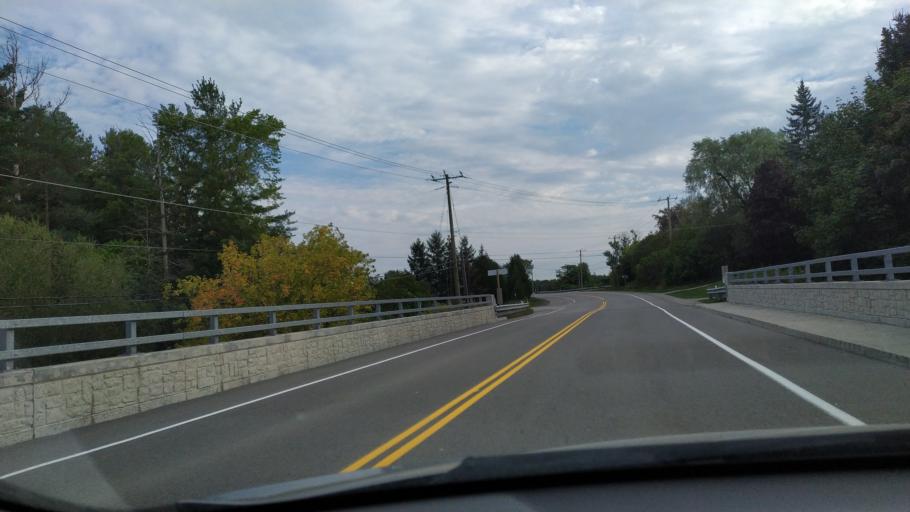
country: CA
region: Ontario
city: Stratford
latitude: 43.4658
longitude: -80.7661
